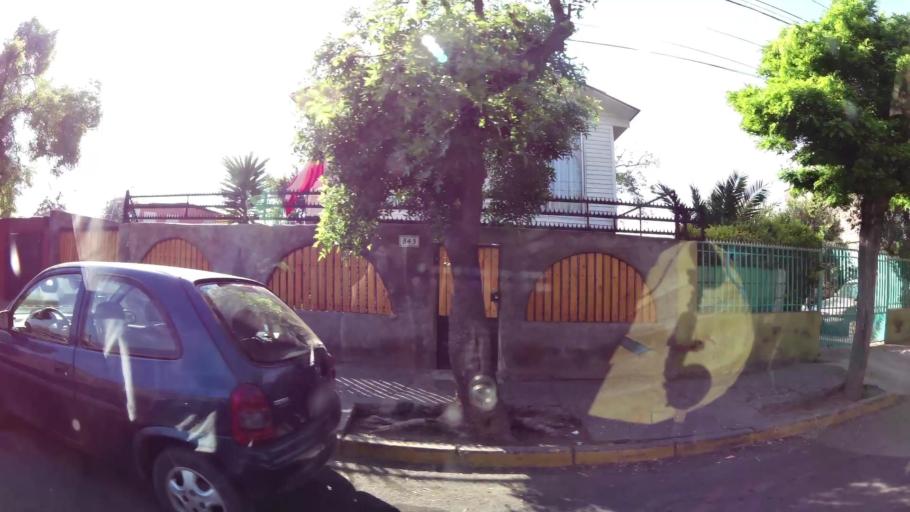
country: CL
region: Santiago Metropolitan
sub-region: Provincia de Maipo
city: San Bernardo
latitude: -33.5964
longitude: -70.7138
